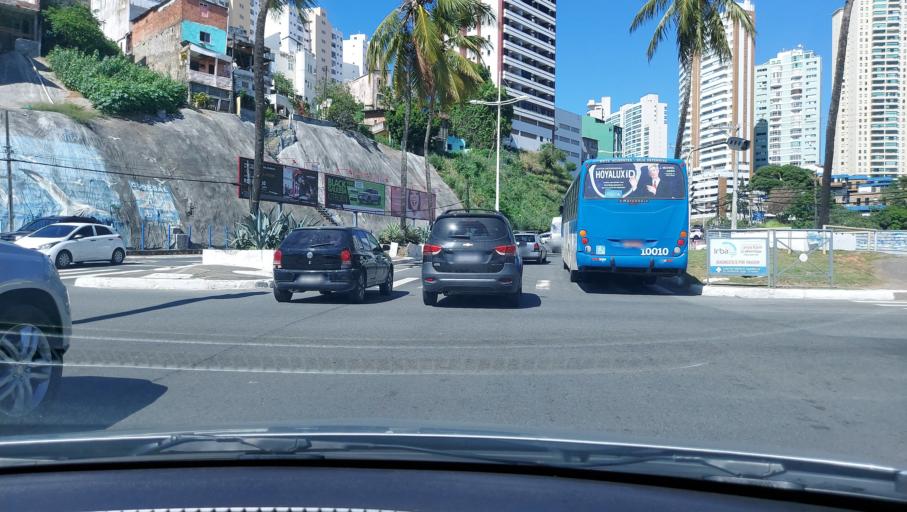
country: BR
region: Bahia
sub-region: Salvador
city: Salvador
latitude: -13.0077
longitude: -38.4926
